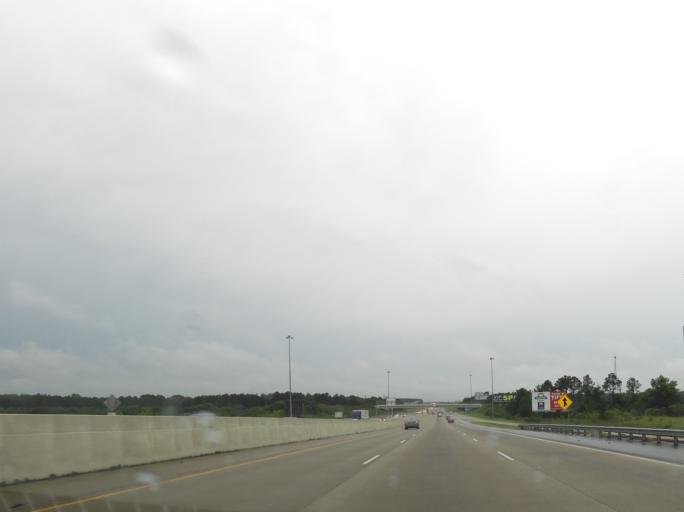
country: US
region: Georgia
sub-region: Crisp County
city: Cordele
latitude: 31.9585
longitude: -83.7515
